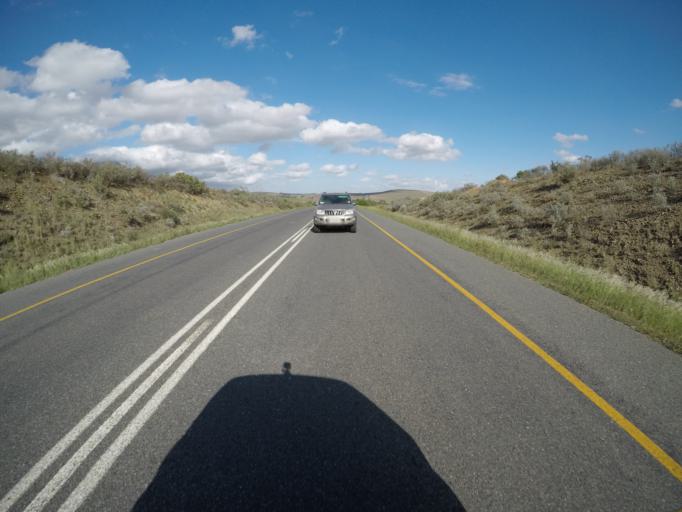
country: ZA
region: Western Cape
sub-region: Cape Winelands District Municipality
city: Ashton
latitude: -33.9550
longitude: 20.2333
